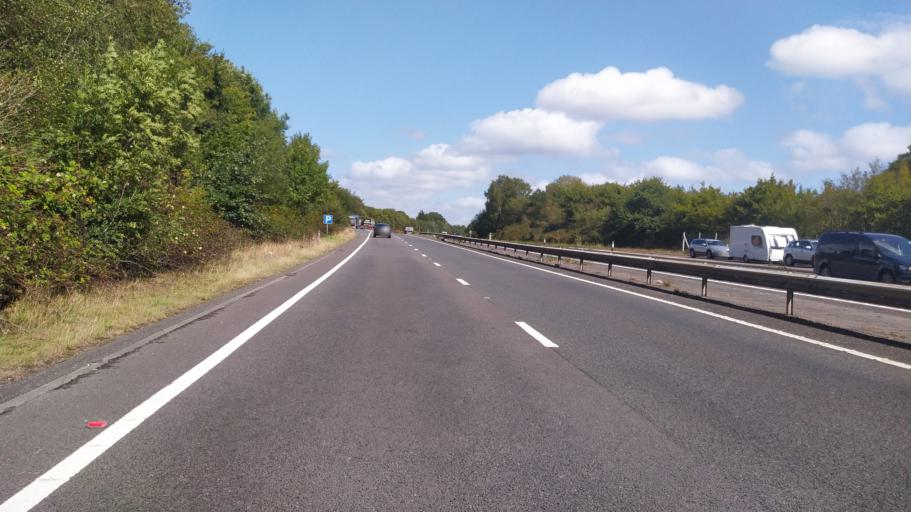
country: GB
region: England
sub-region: Hampshire
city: Petersfield
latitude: 51.0238
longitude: -0.9203
